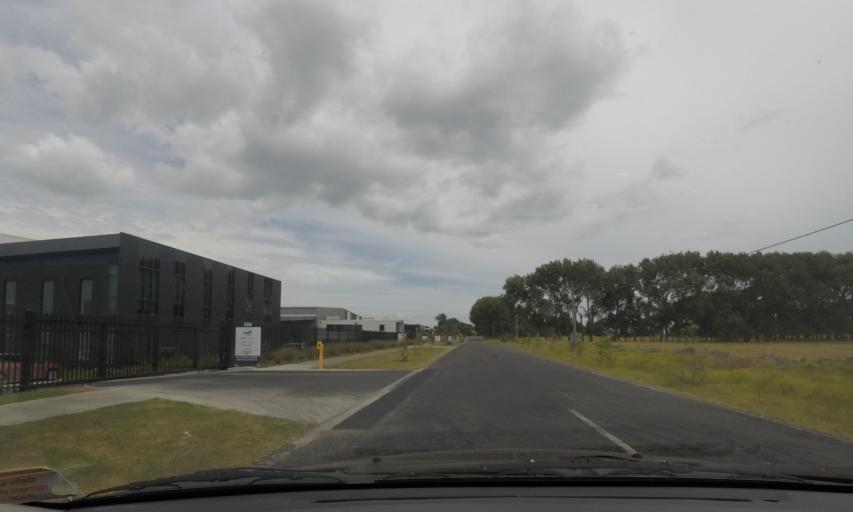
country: NZ
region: Auckland
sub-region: Auckland
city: Mangere
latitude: -36.9891
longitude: 174.7604
